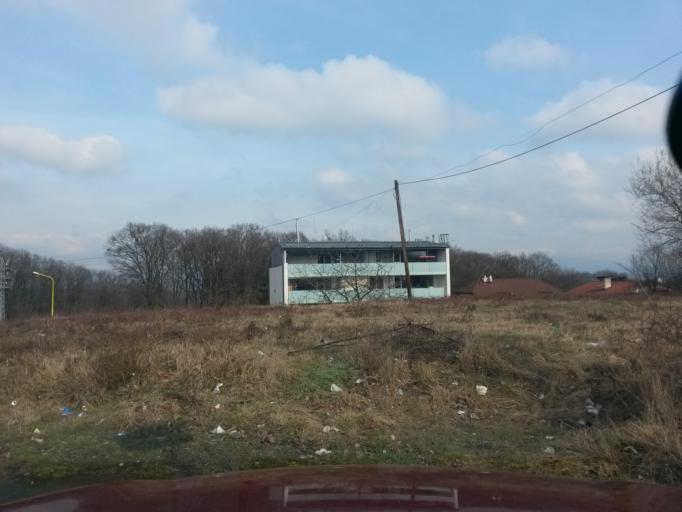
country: SK
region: Kosicky
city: Kosice
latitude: 48.7399
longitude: 21.2916
